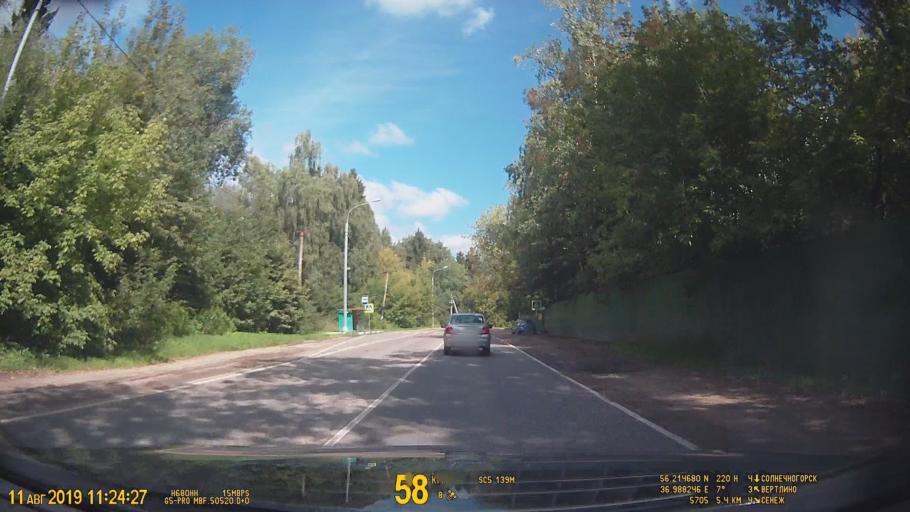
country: RU
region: Moskovskaya
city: Solnechnogorsk
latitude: 56.2151
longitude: 36.9883
